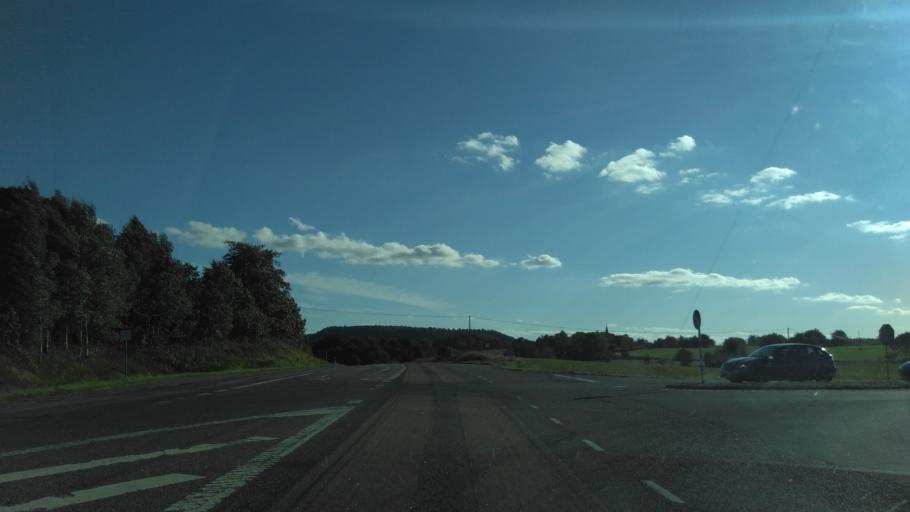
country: SE
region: Vaestra Goetaland
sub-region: Skovde Kommun
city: Skultorp
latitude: 58.3264
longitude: 13.8144
